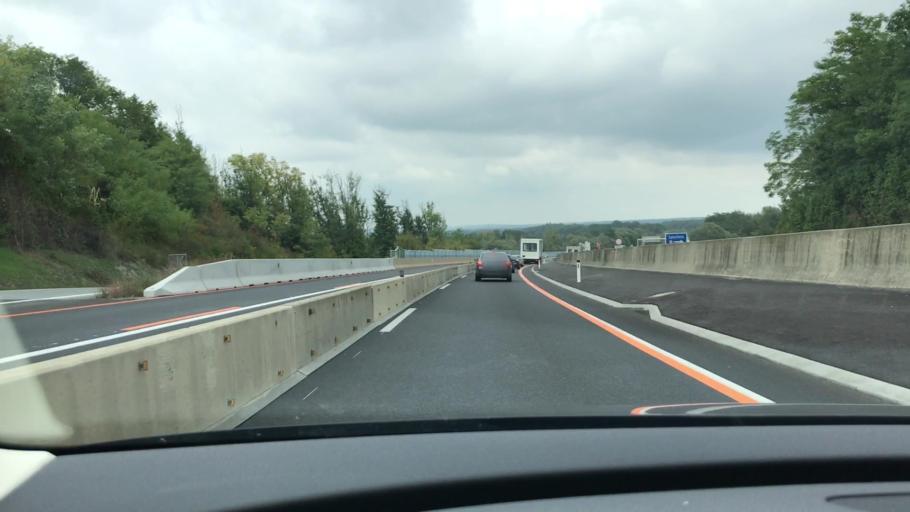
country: AT
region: Styria
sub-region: Politischer Bezirk Leibnitz
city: Spielfeld
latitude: 46.7040
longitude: 15.6380
